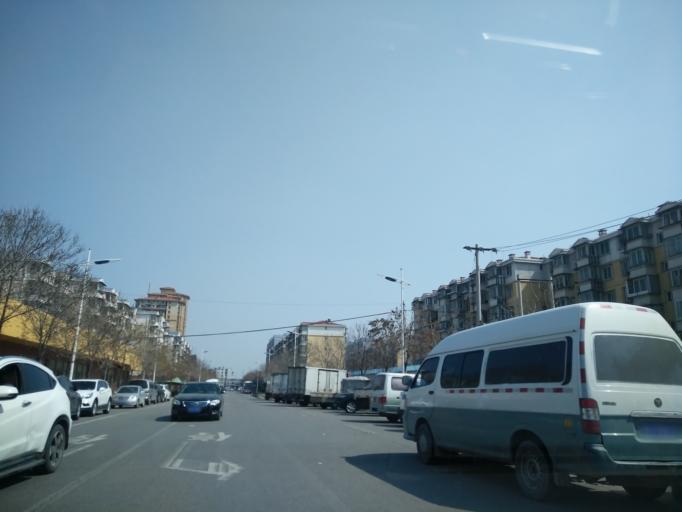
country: CN
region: Beijing
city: Qingyundian
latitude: 39.7572
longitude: 116.5350
